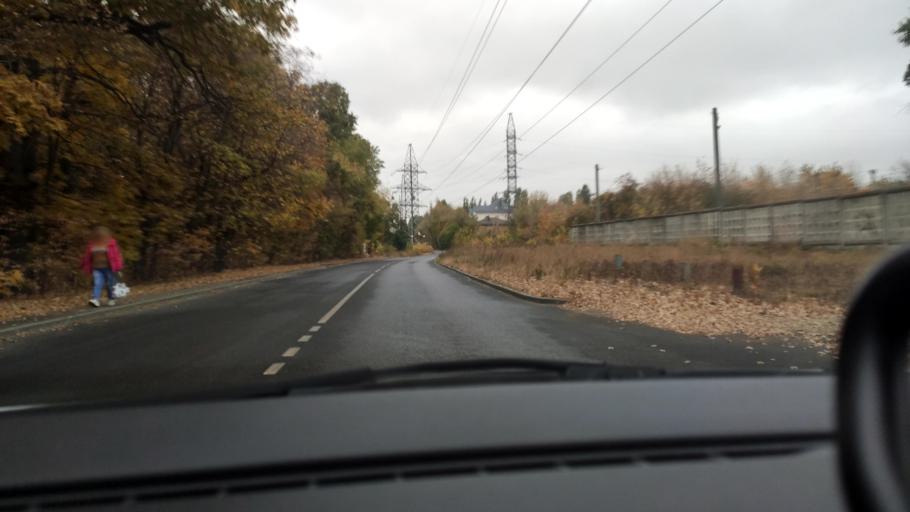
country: RU
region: Voronezj
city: Voronezh
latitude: 51.7164
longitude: 39.2330
